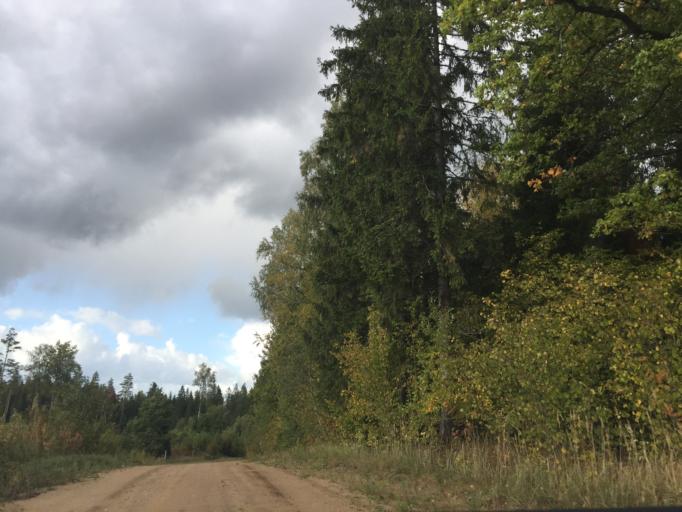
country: LV
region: Ligatne
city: Ligatne
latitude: 57.1003
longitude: 25.1497
